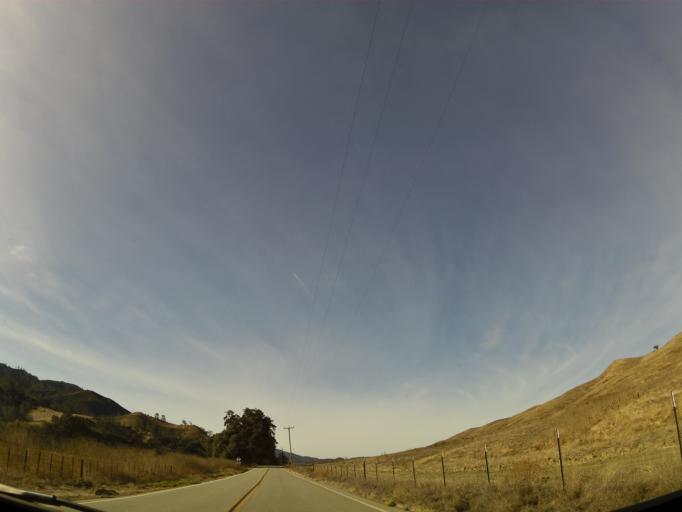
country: US
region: California
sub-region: San Benito County
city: Ridgemark
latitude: 36.7075
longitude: -121.3284
